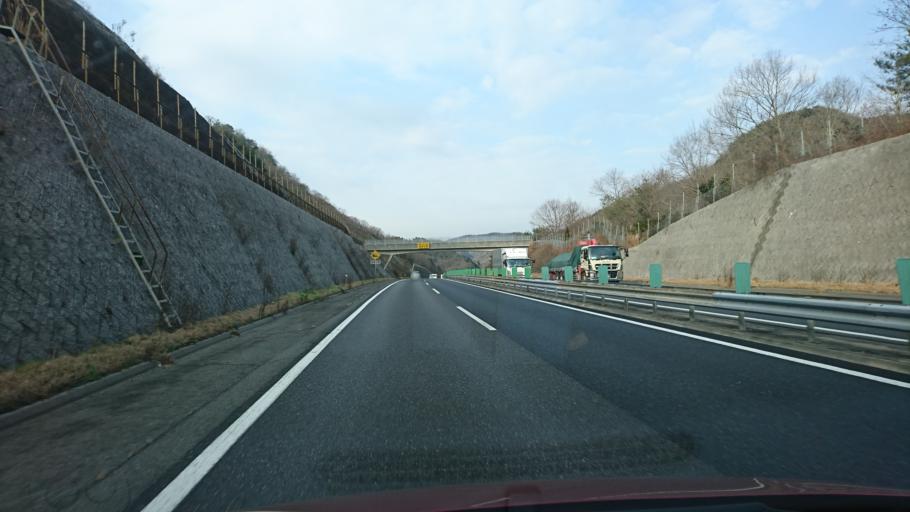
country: JP
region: Hyogo
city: Kariya
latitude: 34.7787
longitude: 134.2340
